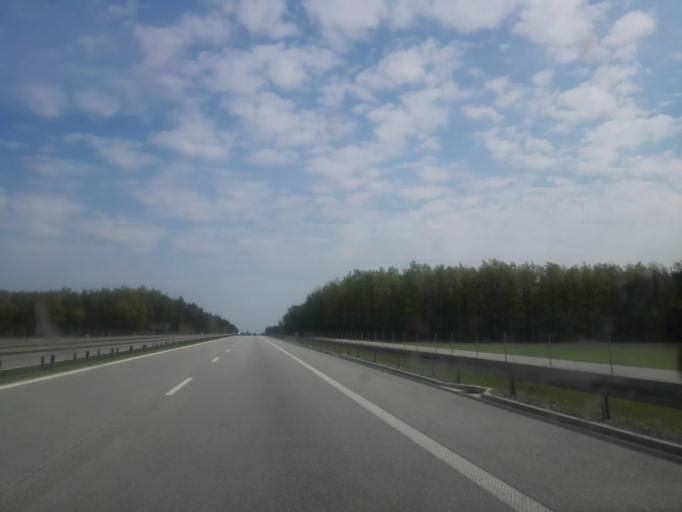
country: PL
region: Lodz Voivodeship
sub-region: Powiat rawski
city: Rawa Mazowiecka
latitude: 51.7196
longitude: 20.2226
